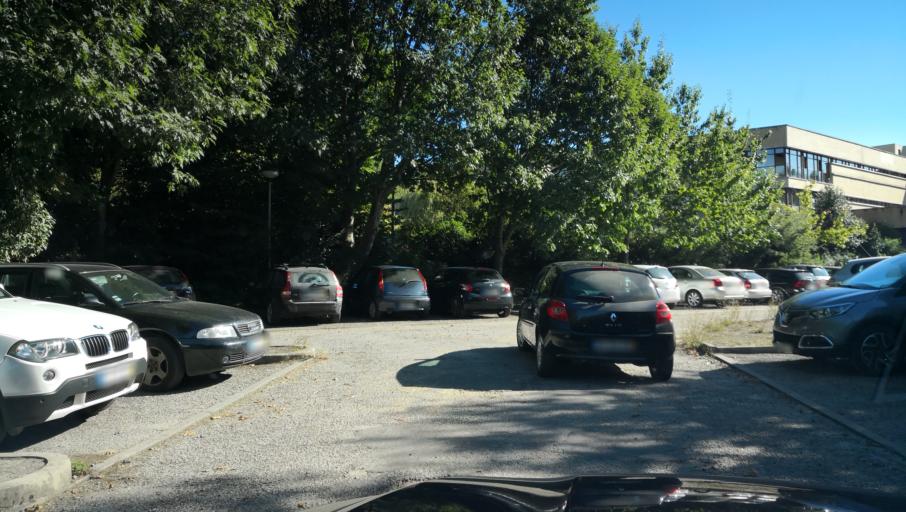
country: PT
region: Vila Real
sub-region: Vila Real
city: Vila Real
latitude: 41.2892
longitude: -7.7409
